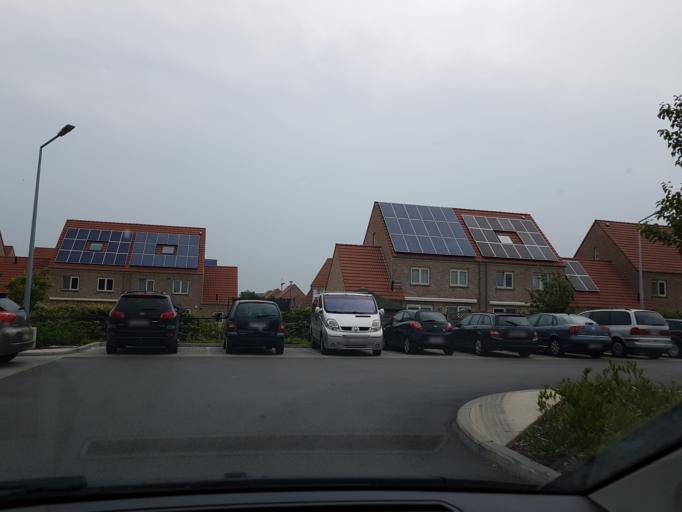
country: BE
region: Flanders
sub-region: Provincie Vlaams-Brabant
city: Steenokkerzeel
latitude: 50.9080
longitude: 4.5137
